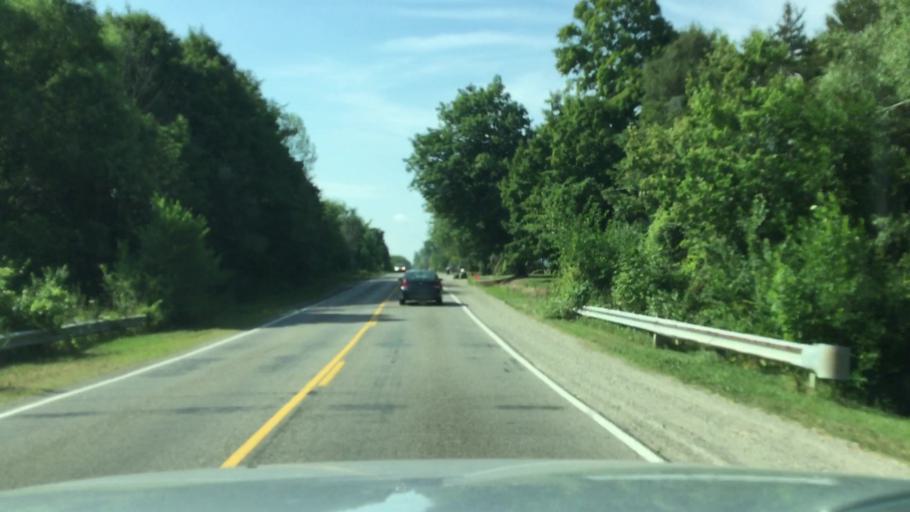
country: US
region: Michigan
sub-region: Genesee County
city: Flushing
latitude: 43.0980
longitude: -83.8136
